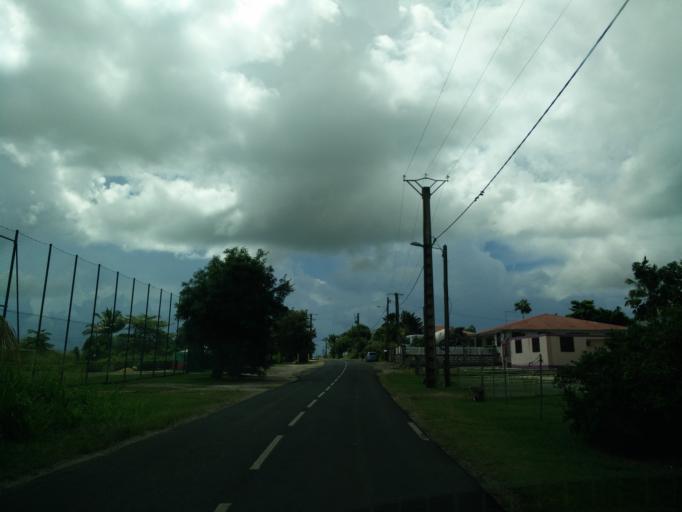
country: GP
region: Guadeloupe
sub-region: Guadeloupe
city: Le Moule
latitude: 16.2940
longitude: -61.3486
